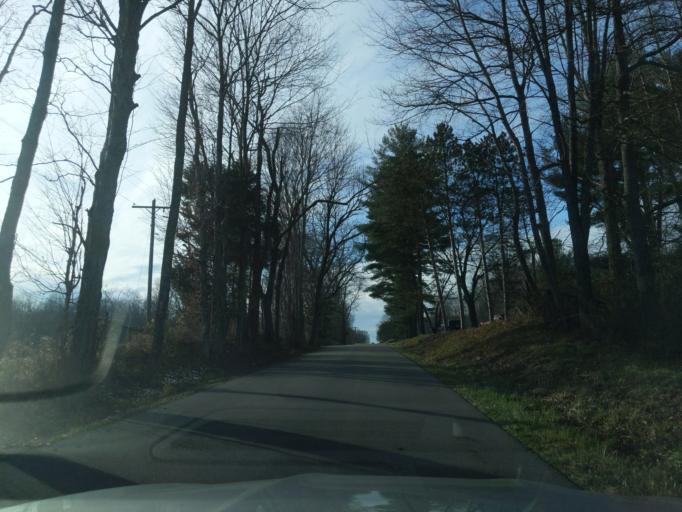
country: US
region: Indiana
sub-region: Decatur County
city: Westport
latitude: 39.1904
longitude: -85.5149
